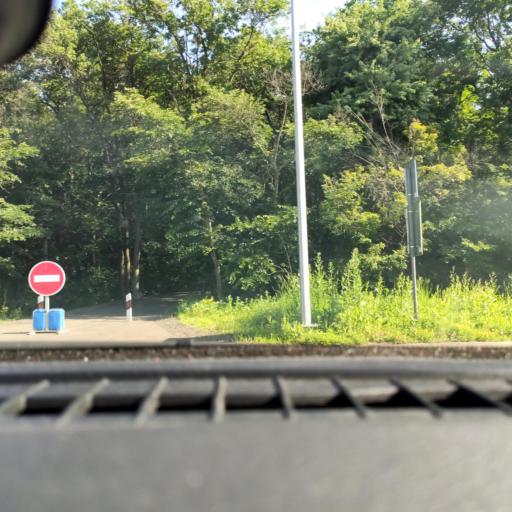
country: RU
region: Voronezj
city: Somovo
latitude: 51.6870
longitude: 39.3387
